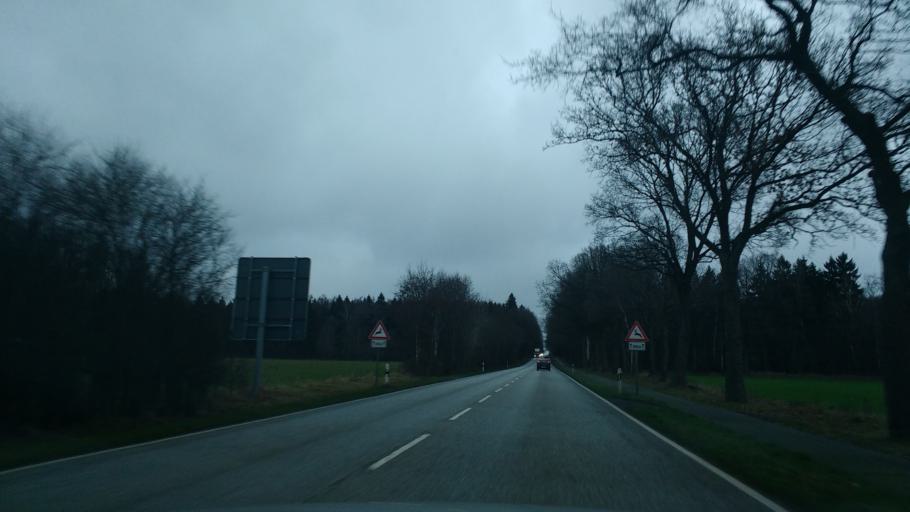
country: DE
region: Schleswig-Holstein
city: Peissen
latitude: 54.0051
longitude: 9.5872
